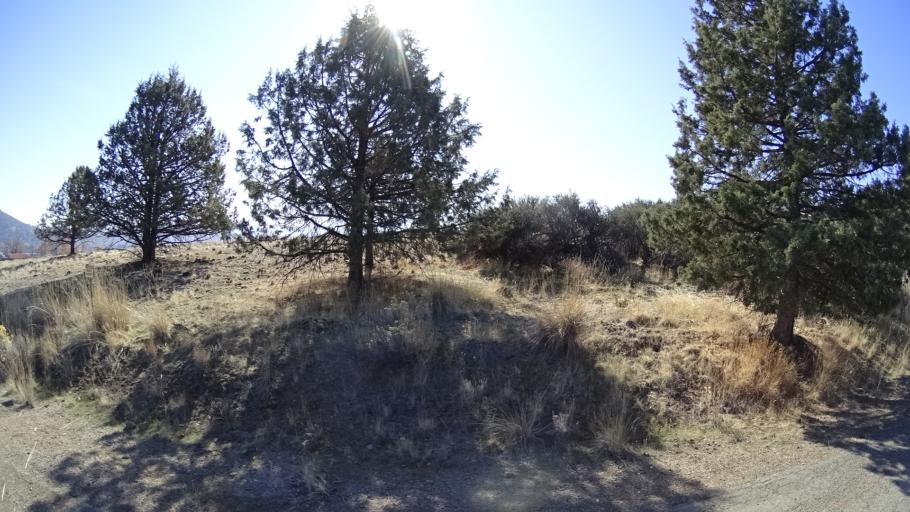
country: US
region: California
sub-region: Siskiyou County
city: Yreka
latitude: 41.7287
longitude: -122.6502
